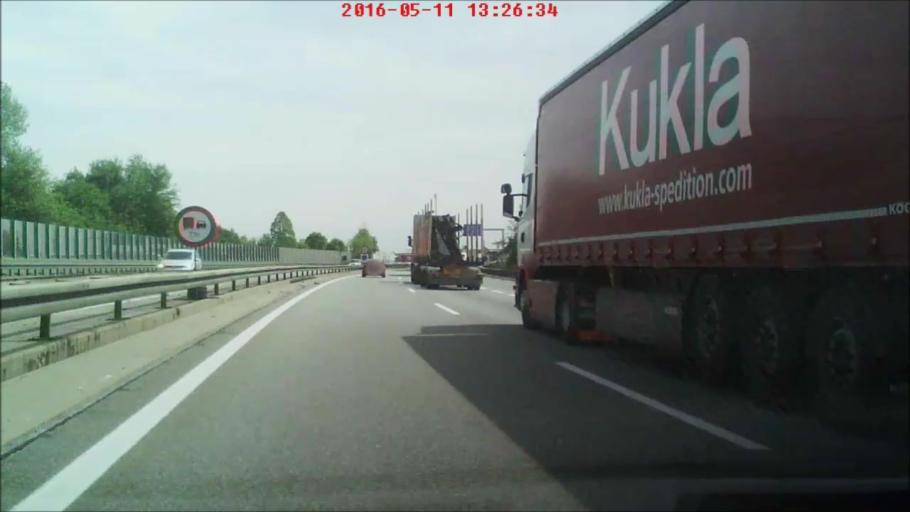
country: AT
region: Upper Austria
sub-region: Politischer Bezirk Scharding
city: Sankt Florian am Inn
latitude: 48.4110
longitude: 13.4257
